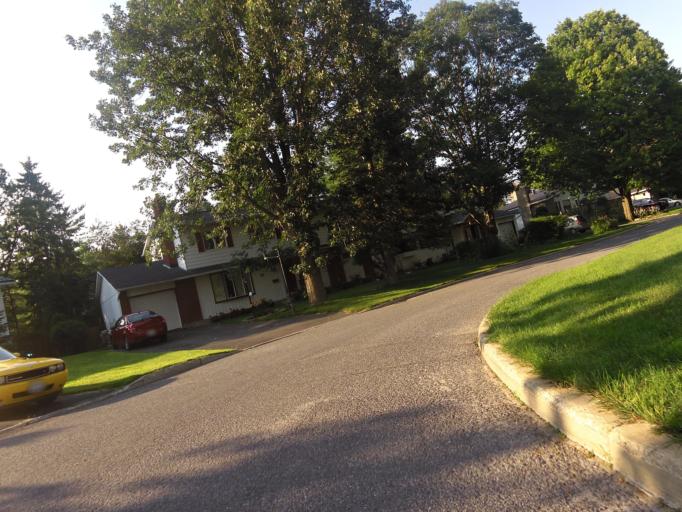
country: CA
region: Ontario
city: Bells Corners
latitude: 45.3304
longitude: -75.7889
